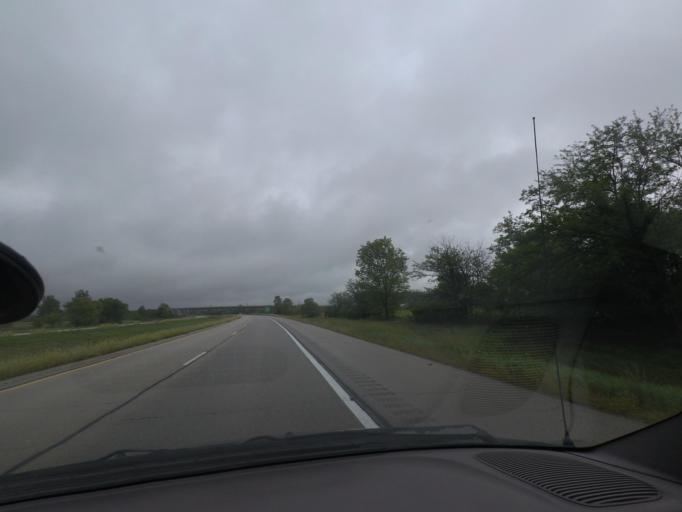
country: US
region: Illinois
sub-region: Piatt County
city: Monticello
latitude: 40.0914
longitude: -88.5079
